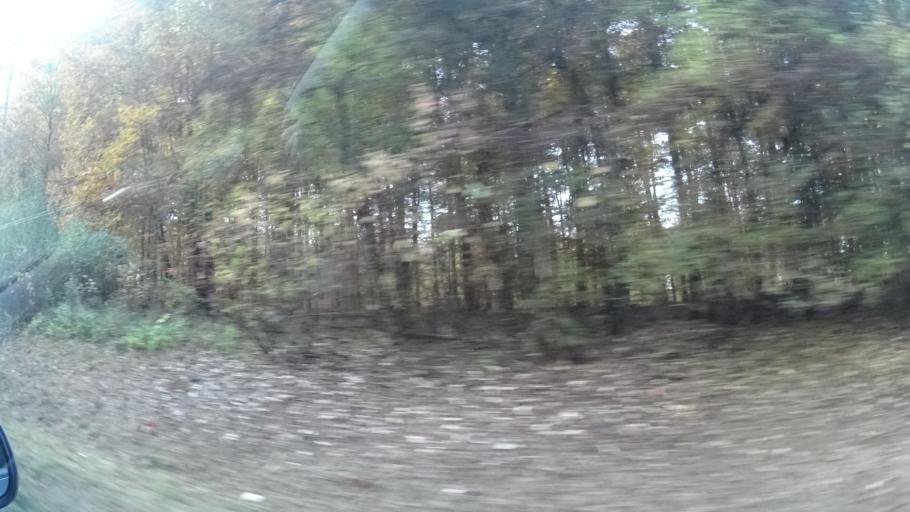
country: DE
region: Baden-Wuerttemberg
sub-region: Karlsruhe Region
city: Binau
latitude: 49.3548
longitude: 9.0620
